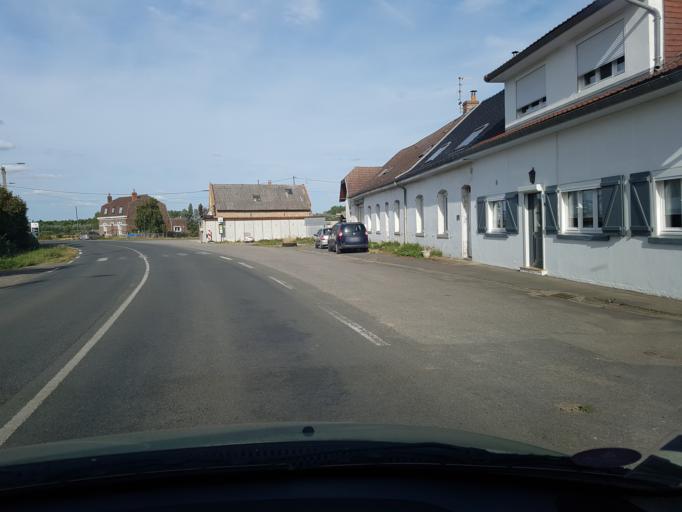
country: FR
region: Nord-Pas-de-Calais
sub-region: Departement du Pas-de-Calais
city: Lestrem
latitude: 50.5979
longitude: 2.6904
